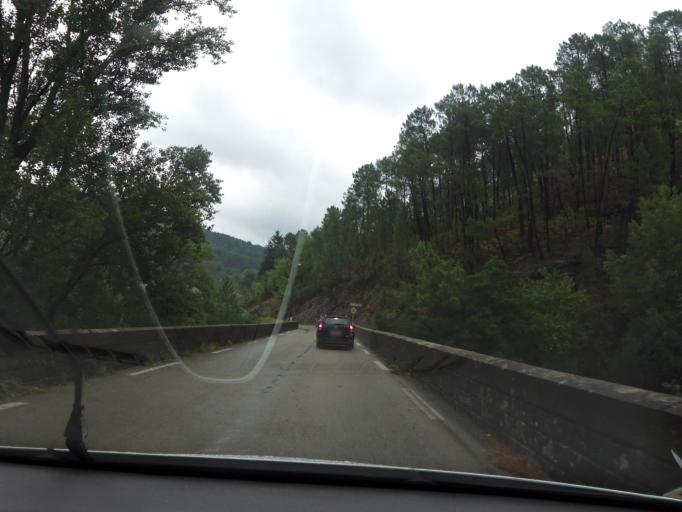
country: FR
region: Languedoc-Roussillon
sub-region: Departement du Gard
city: Branoux-les-Taillades
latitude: 44.2301
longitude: 3.9998
